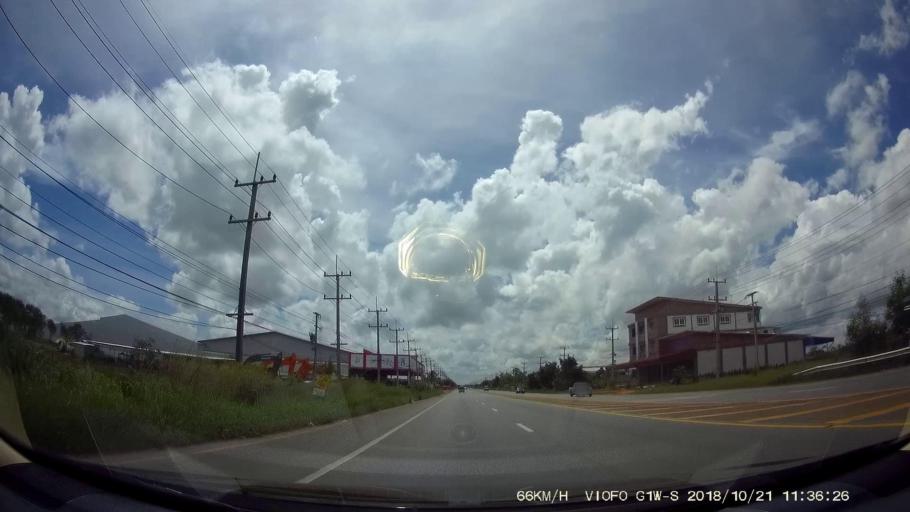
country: TH
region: Chaiyaphum
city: Chaiyaphum
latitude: 15.7195
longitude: 102.0162
